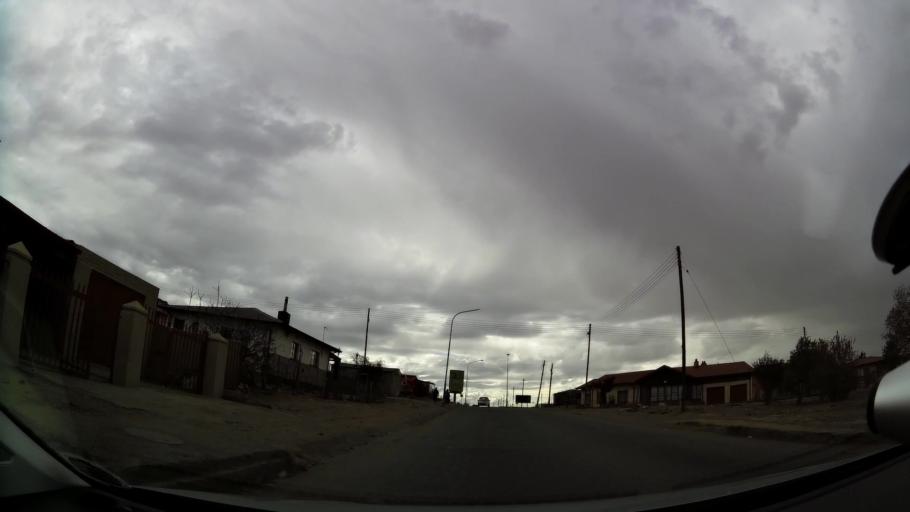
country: ZA
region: Orange Free State
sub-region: Fezile Dabi District Municipality
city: Kroonstad
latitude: -27.6526
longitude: 27.1994
